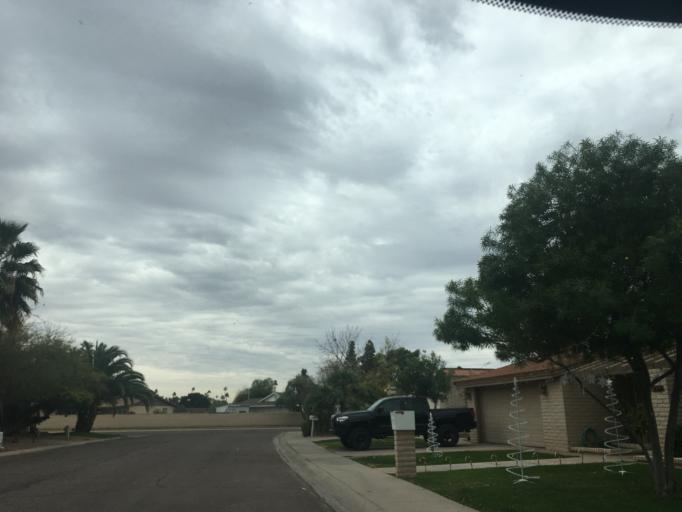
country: US
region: Arizona
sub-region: Maricopa County
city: Guadalupe
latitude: 33.3717
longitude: -111.9256
